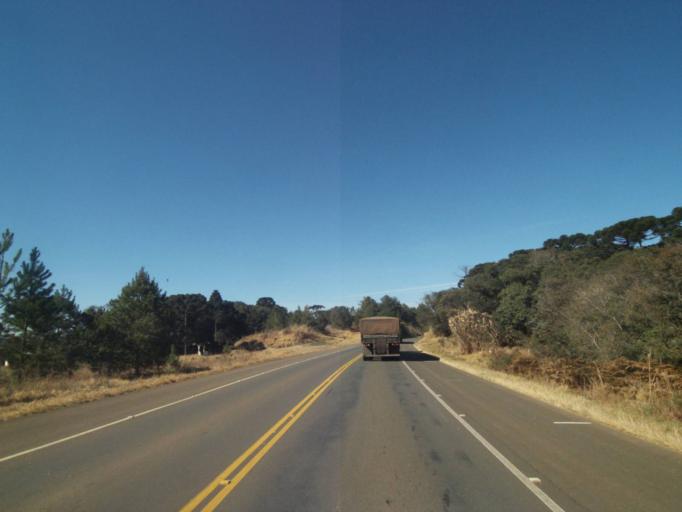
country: BR
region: Parana
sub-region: Tibagi
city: Tibagi
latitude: -24.5830
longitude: -50.4384
